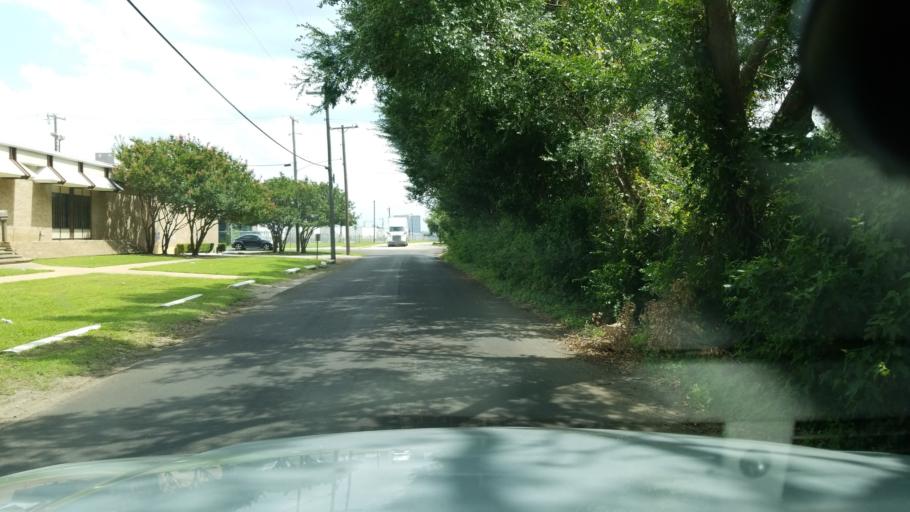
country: US
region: Texas
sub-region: Dallas County
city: University Park
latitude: 32.8303
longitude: -96.8623
